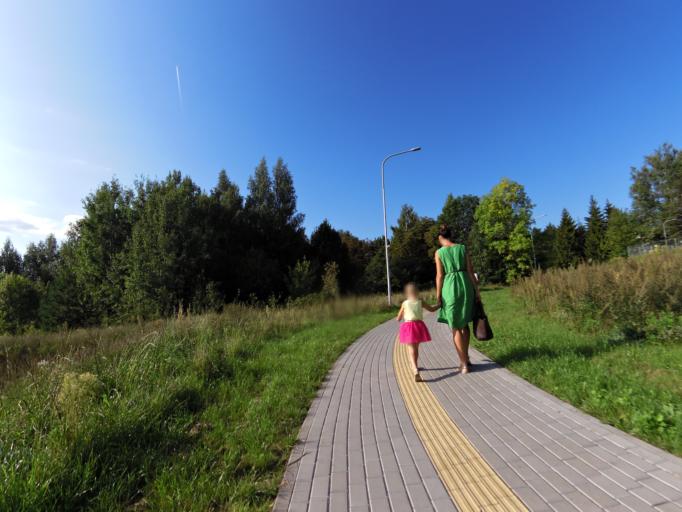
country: LT
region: Vilnius County
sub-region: Vilnius
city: Fabijoniskes
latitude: 54.7558
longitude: 25.2861
